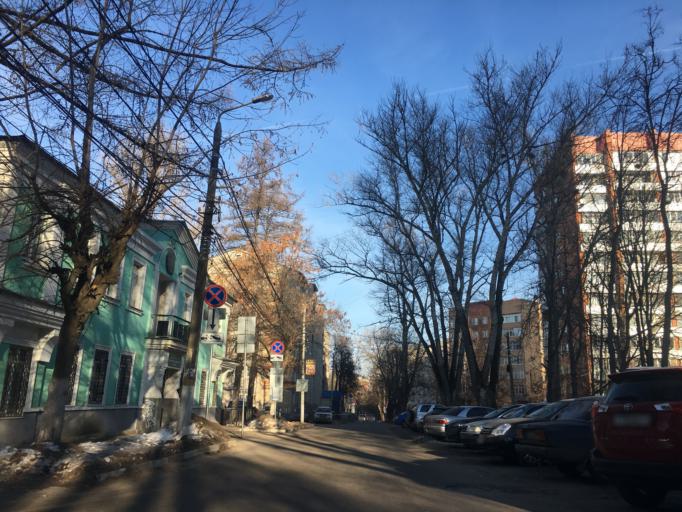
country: RU
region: Tula
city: Tula
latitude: 54.1886
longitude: 37.5870
